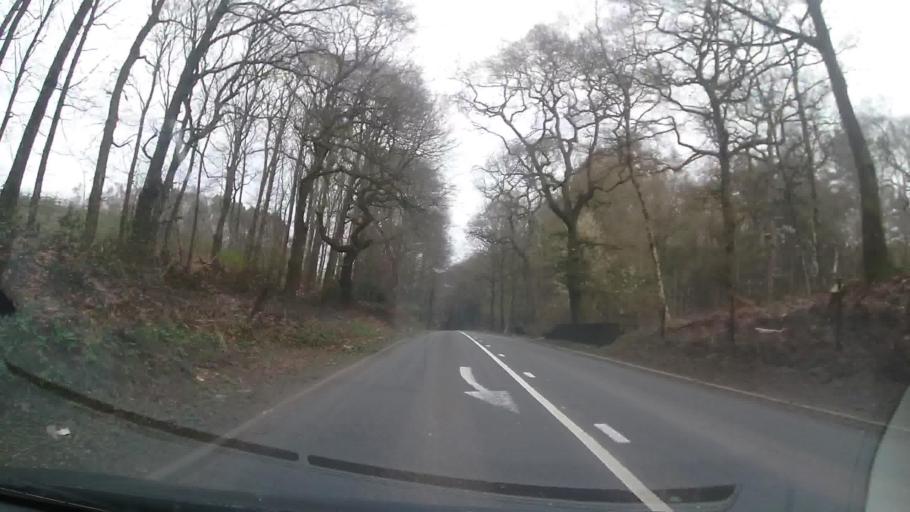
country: GB
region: England
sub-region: Staffordshire
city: Standon
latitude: 52.9519
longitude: -2.3241
